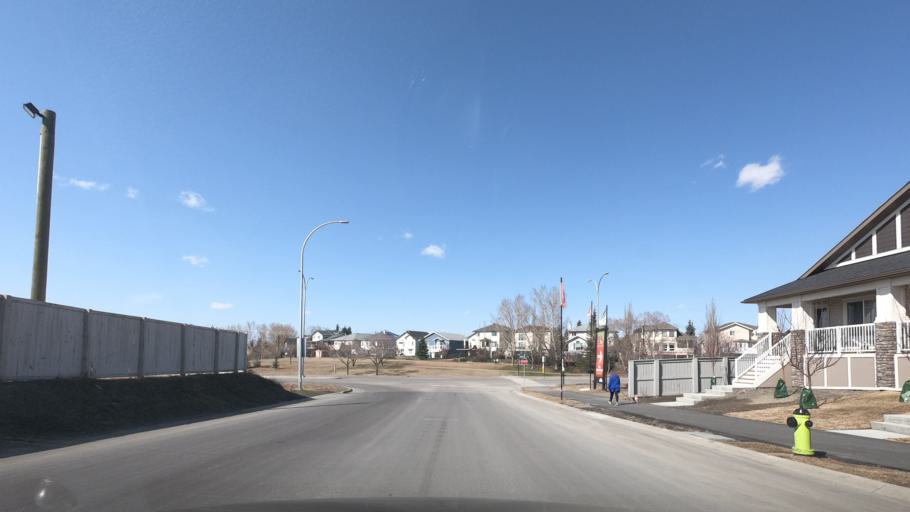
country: CA
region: Alberta
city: Airdrie
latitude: 51.2702
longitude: -113.9816
